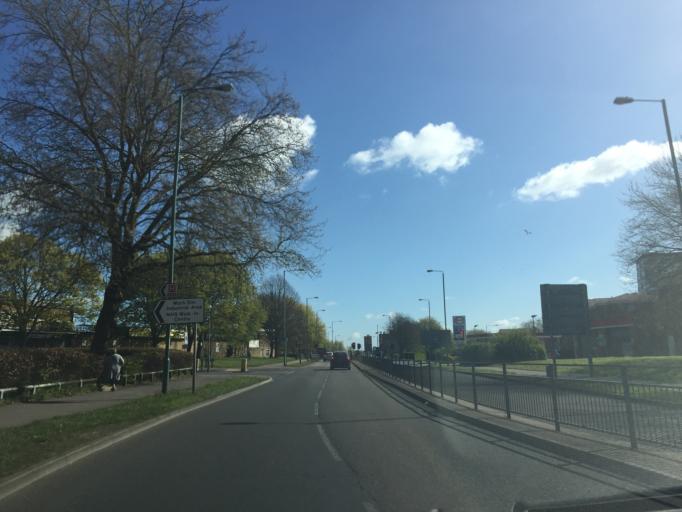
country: GB
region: England
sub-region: Essex
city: Harlow
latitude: 51.7707
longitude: 0.0893
